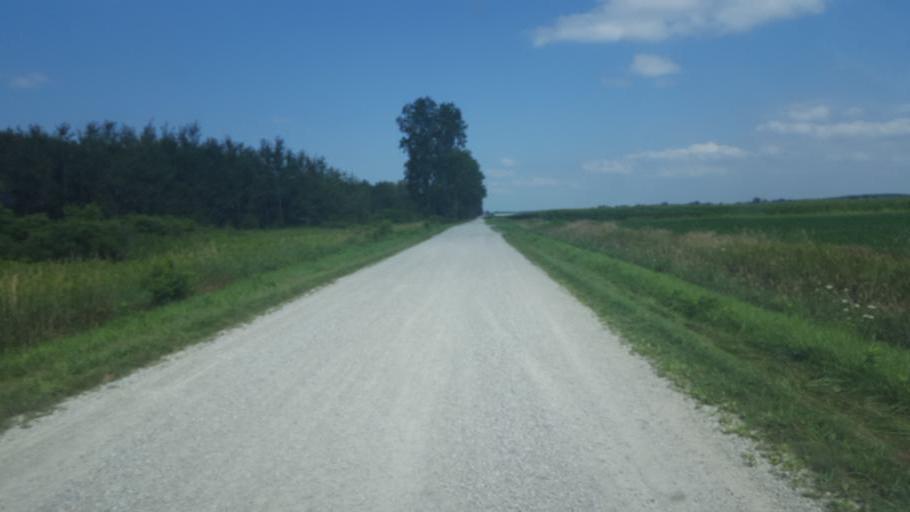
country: US
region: Ohio
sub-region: Huron County
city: Willard
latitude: 40.9959
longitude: -82.7640
